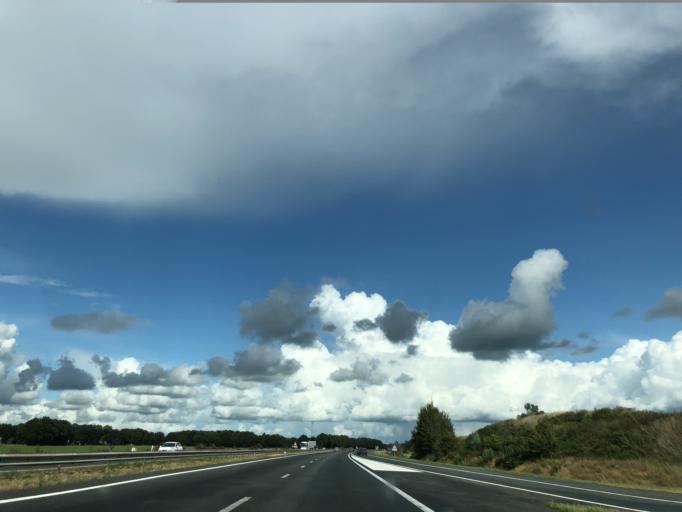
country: NL
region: Friesland
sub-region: Gemeente Smallingerland
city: Drachtstercompagnie
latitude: 53.1307
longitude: 6.1892
